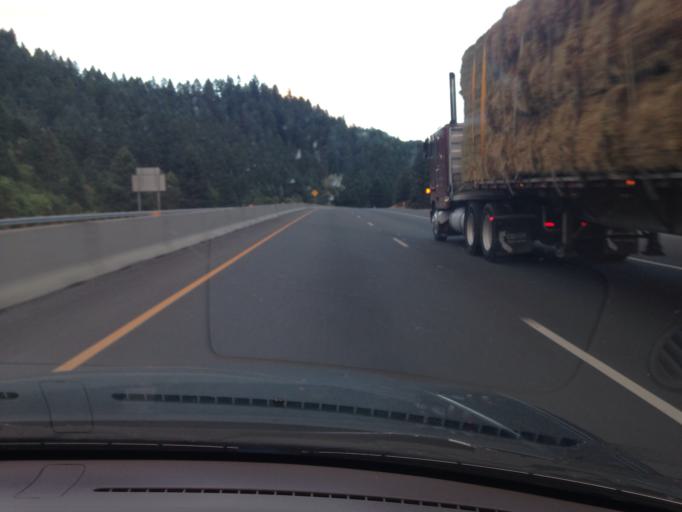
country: US
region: Oregon
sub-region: Douglas County
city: Canyonville
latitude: 42.7319
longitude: -123.3705
